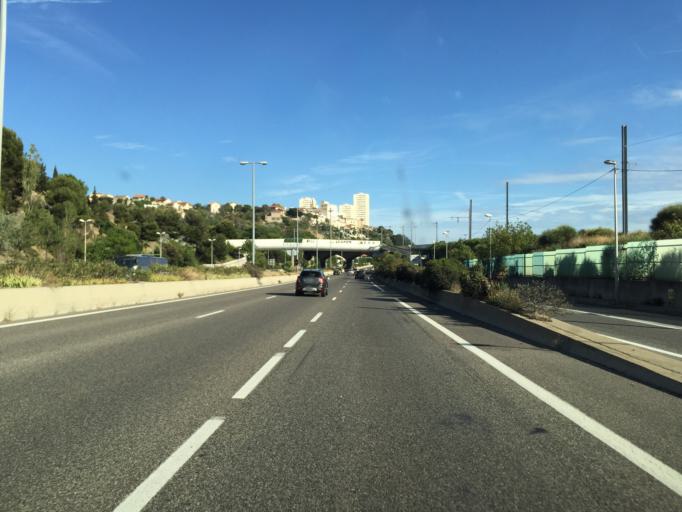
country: FR
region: Provence-Alpes-Cote d'Azur
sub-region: Departement des Bouches-du-Rhone
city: Marseille 16
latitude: 43.3451
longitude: 5.3461
